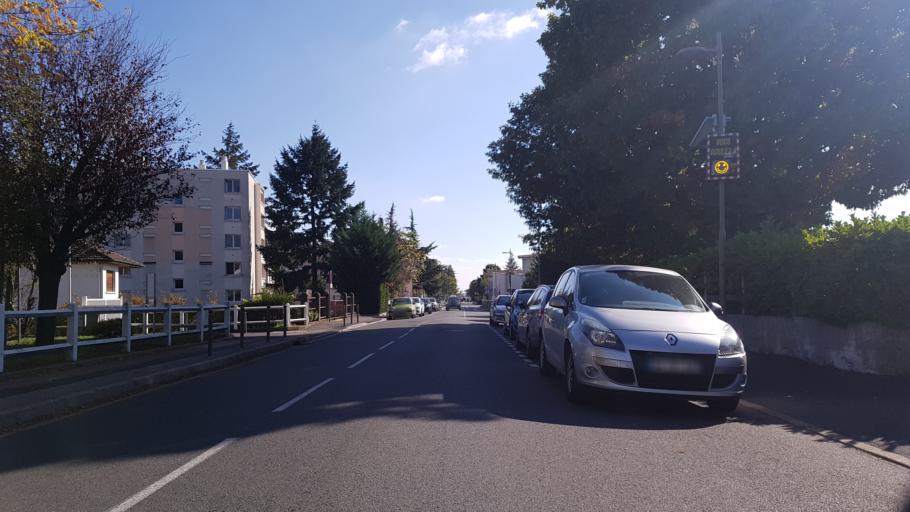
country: FR
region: Rhone-Alpes
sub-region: Departement du Rhone
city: Ecully
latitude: 45.7969
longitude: 4.7872
